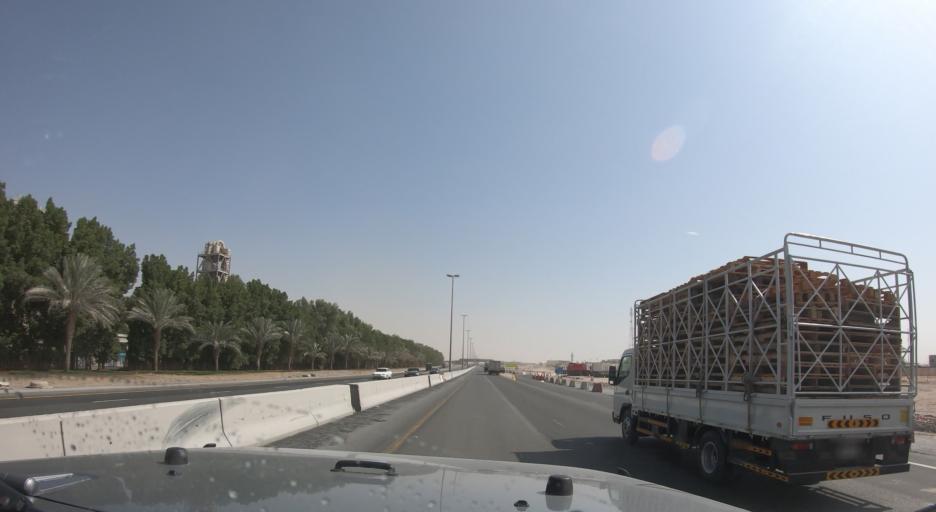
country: AE
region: Ash Shariqah
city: Sharjah
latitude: 25.2944
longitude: 55.6136
